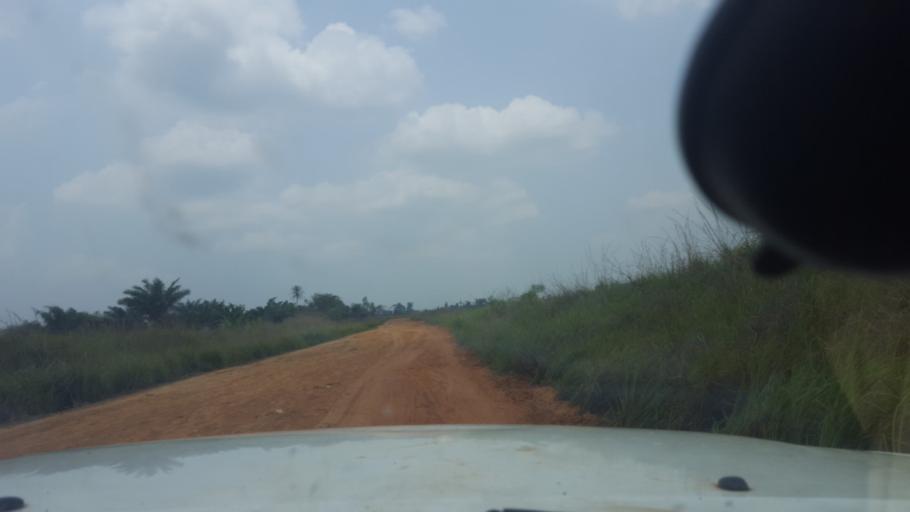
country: CD
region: Bandundu
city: Bandundu
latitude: -3.3276
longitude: 17.2898
